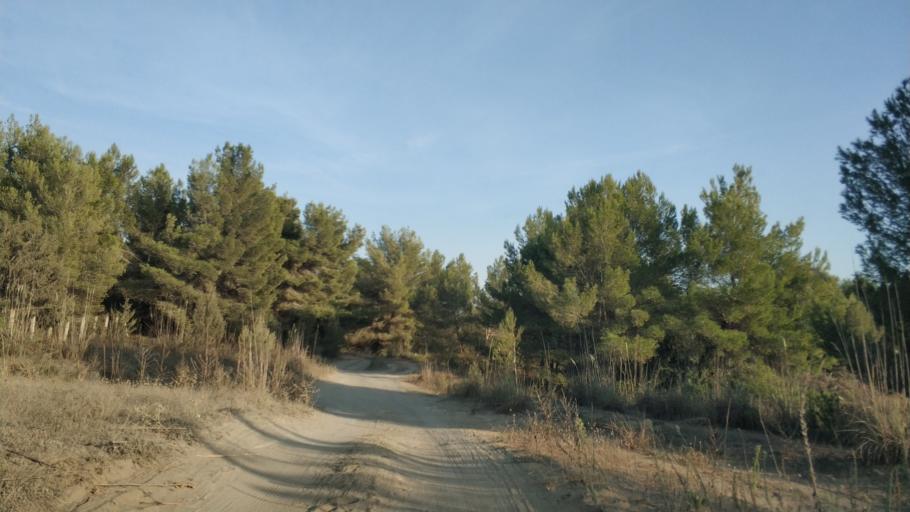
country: AL
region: Fier
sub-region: Rrethi i Lushnjes
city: Divjake
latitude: 40.9536
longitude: 19.4733
